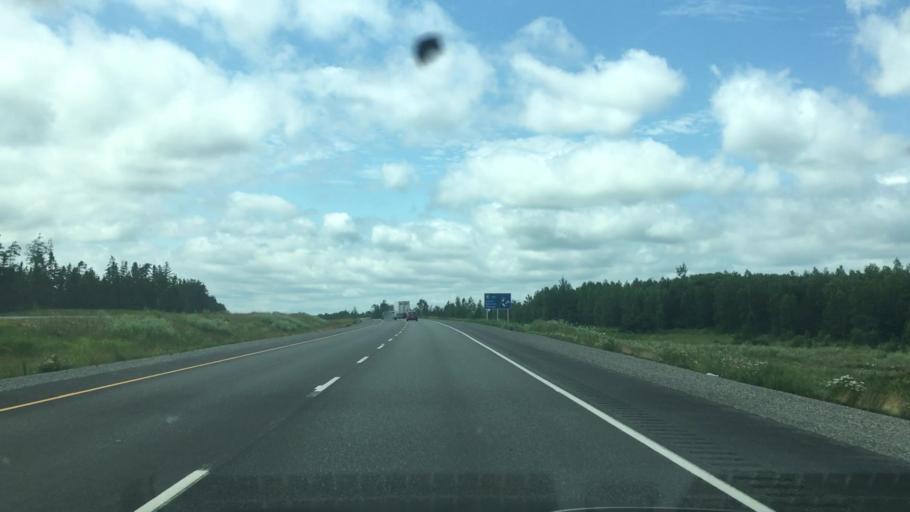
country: CA
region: Nova Scotia
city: Springhill
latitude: 45.7060
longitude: -63.9701
